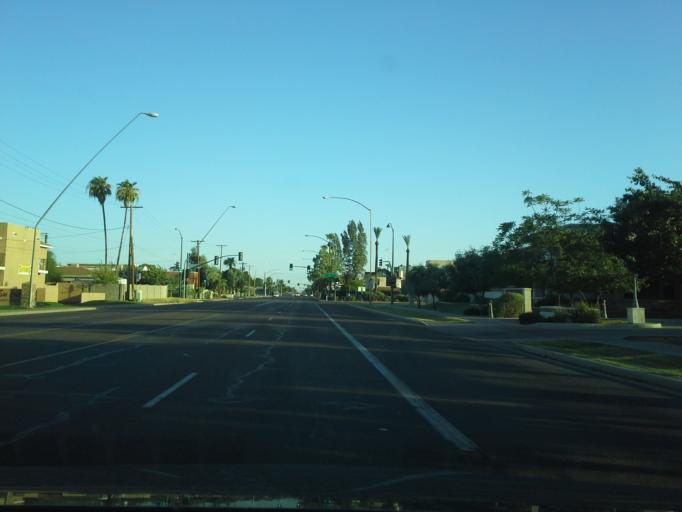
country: US
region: Arizona
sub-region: Maricopa County
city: Mesa
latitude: 33.4183
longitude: -111.8230
